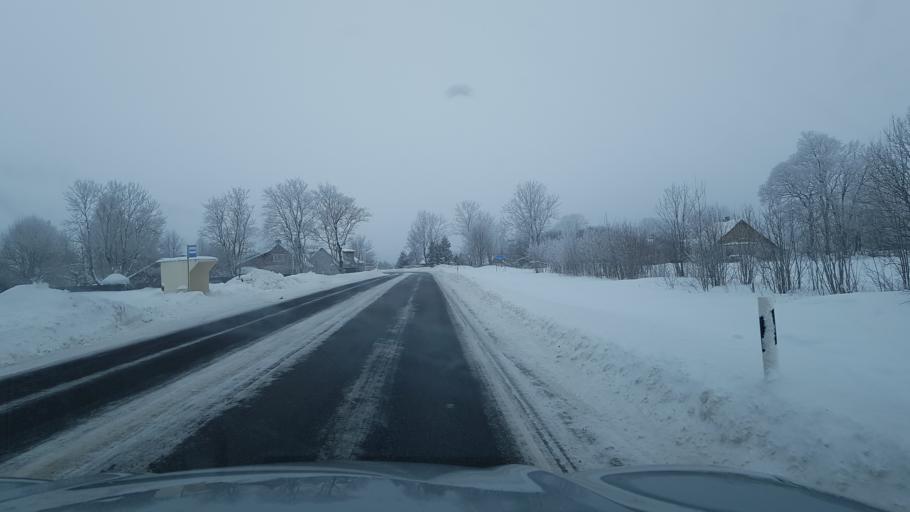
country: EE
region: Ida-Virumaa
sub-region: Johvi vald
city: Johvi
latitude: 59.3196
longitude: 27.3948
